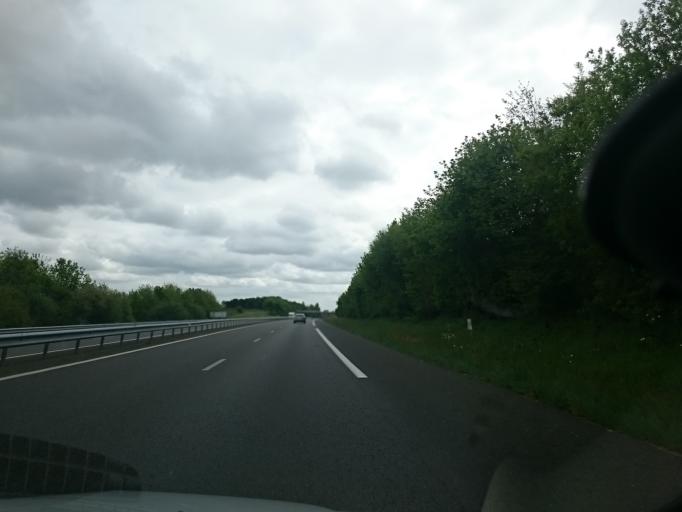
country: FR
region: Brittany
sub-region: Departement d'Ille-et-Vilaine
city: Saint-Sauveur-des-Landes
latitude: 48.3725
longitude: -1.3033
